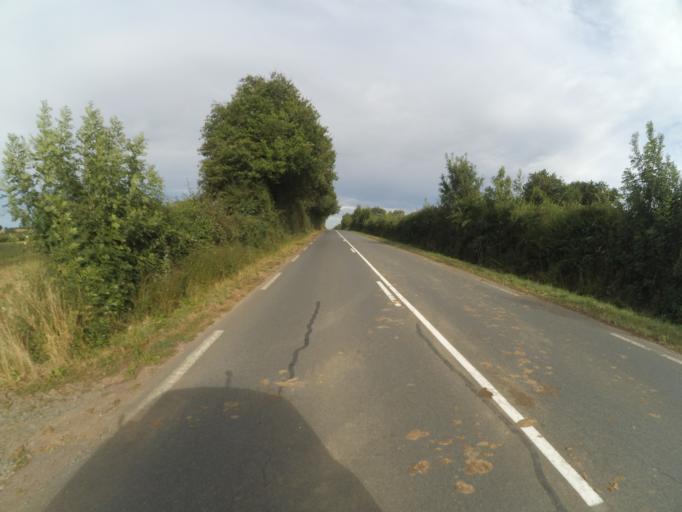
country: FR
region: Poitou-Charentes
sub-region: Departement des Deux-Sevres
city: Saint-Amand-sur-Sevre
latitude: 46.9273
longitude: -0.7694
